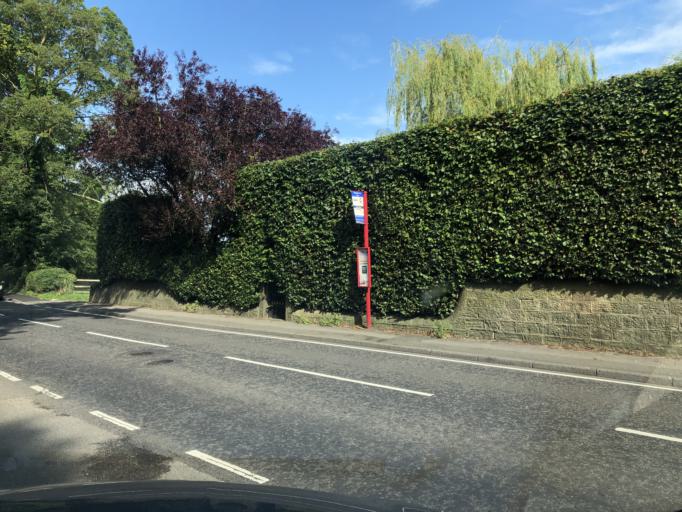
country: GB
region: England
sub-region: City and Borough of Leeds
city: Pool
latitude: 53.8994
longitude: -1.6162
